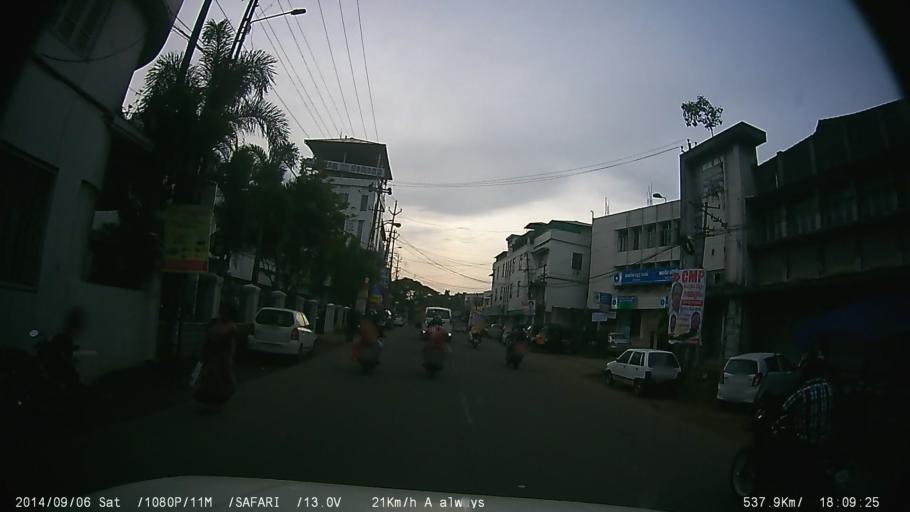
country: IN
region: Kerala
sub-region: Kottayam
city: Kottayam
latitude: 9.5888
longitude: 76.5286
